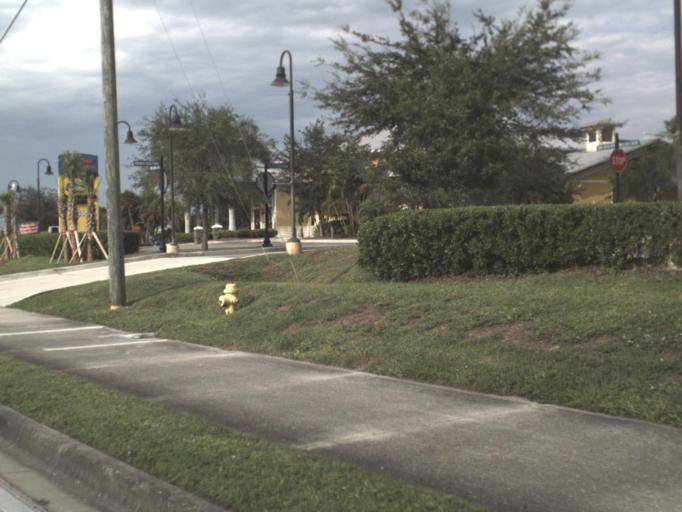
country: US
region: Florida
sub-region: Lee County
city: Fort Myers Beach
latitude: 26.4848
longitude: -81.9438
